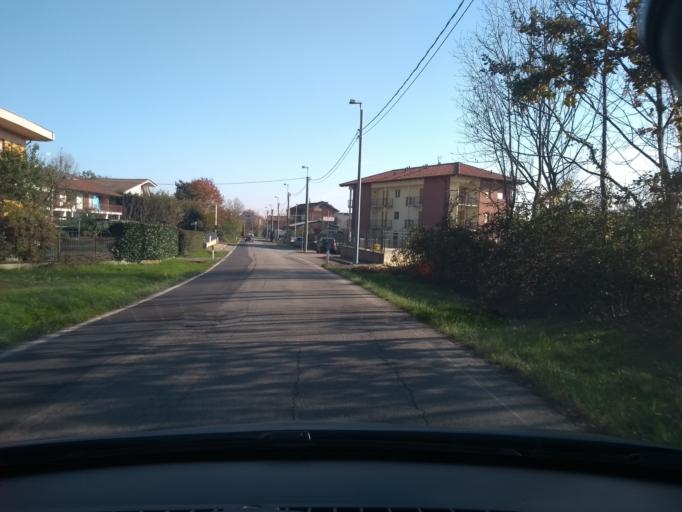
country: IT
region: Piedmont
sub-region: Provincia di Torino
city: Robassomero
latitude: 45.2039
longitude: 7.5593
